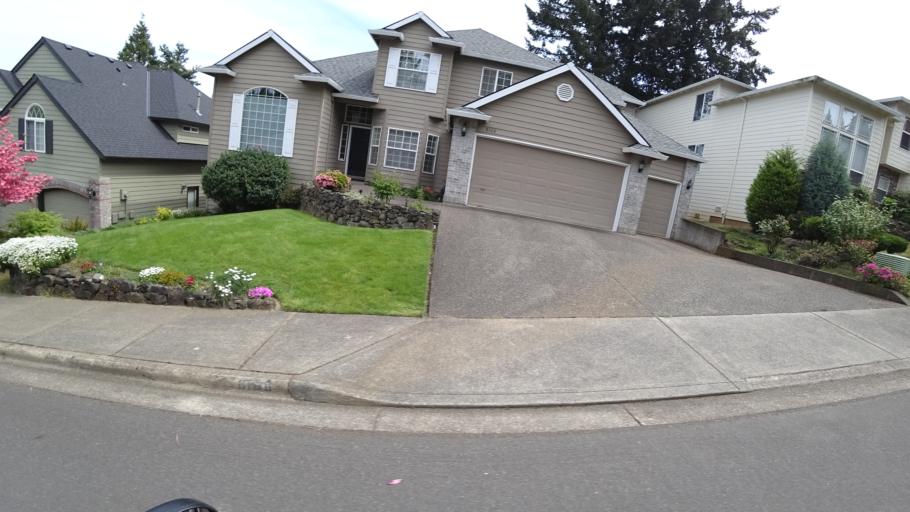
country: US
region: Oregon
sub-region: Washington County
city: Aloha
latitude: 45.4607
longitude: -122.8529
